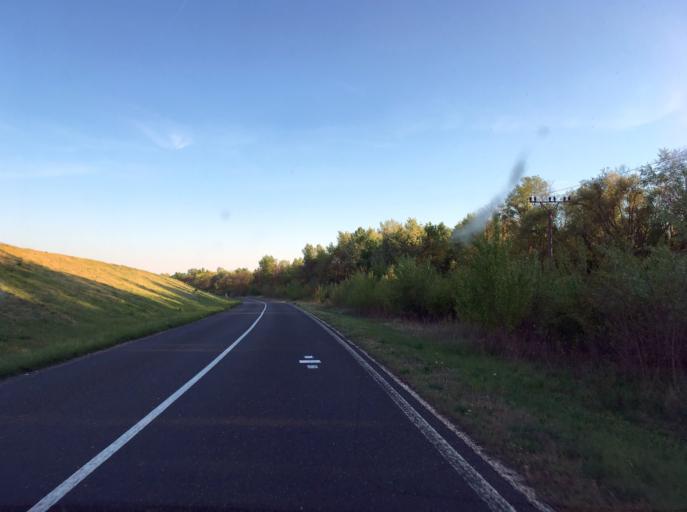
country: HU
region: Gyor-Moson-Sopron
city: Rajka
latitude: 48.0079
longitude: 17.2520
